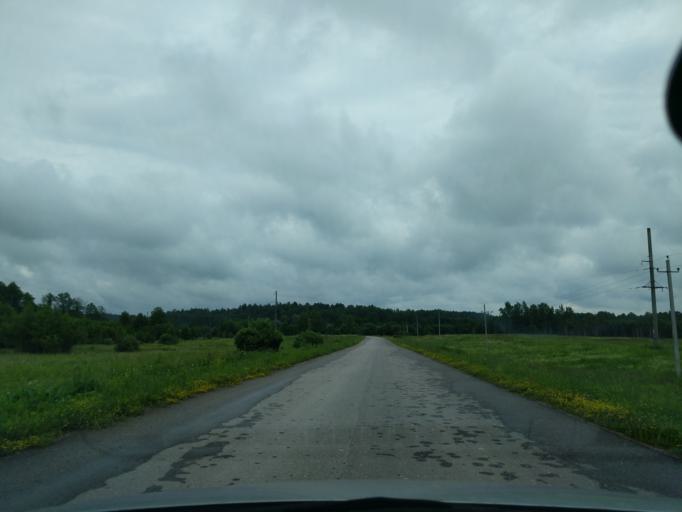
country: RU
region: Kaluga
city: Myatlevo
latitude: 54.8139
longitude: 35.6774
